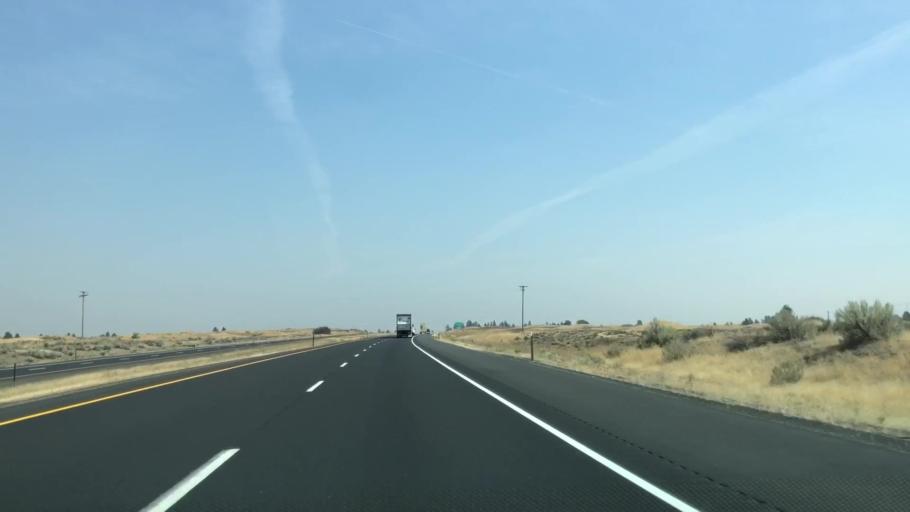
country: US
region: Washington
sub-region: Spokane County
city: Medical Lake
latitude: 47.3822
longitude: -117.8630
